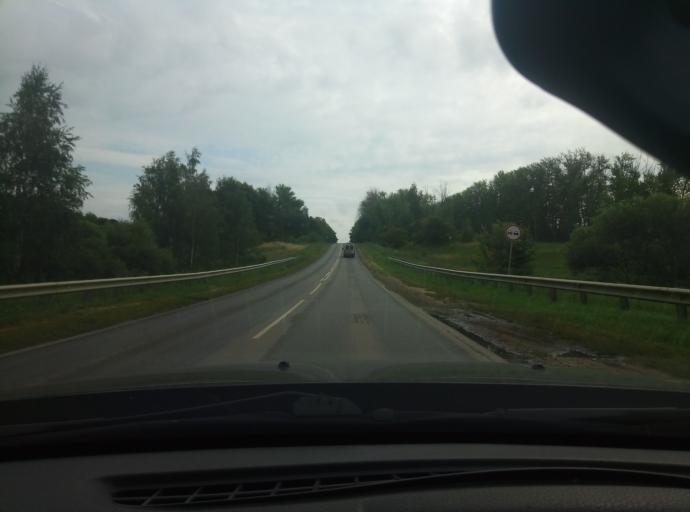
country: RU
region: Tula
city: Donskoy
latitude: 53.9692
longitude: 38.3861
